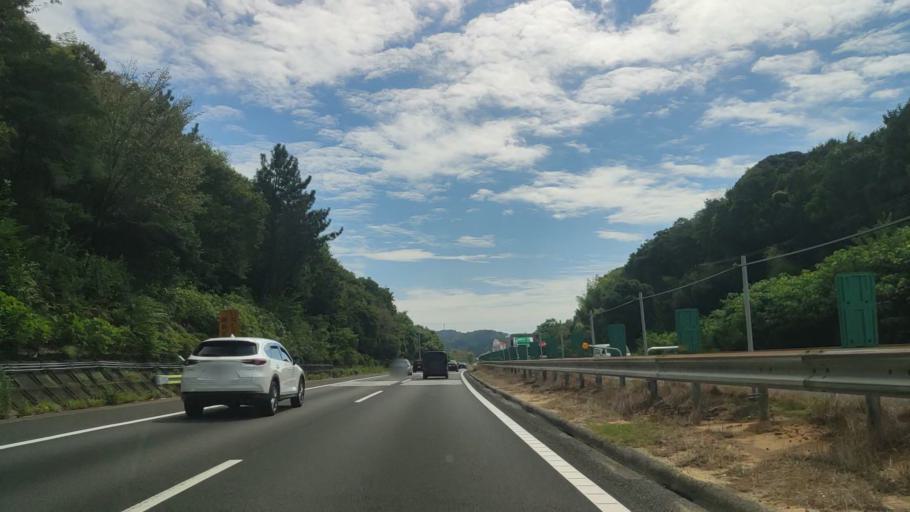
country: JP
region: Aichi
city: Okazaki
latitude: 34.9951
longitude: 137.1826
